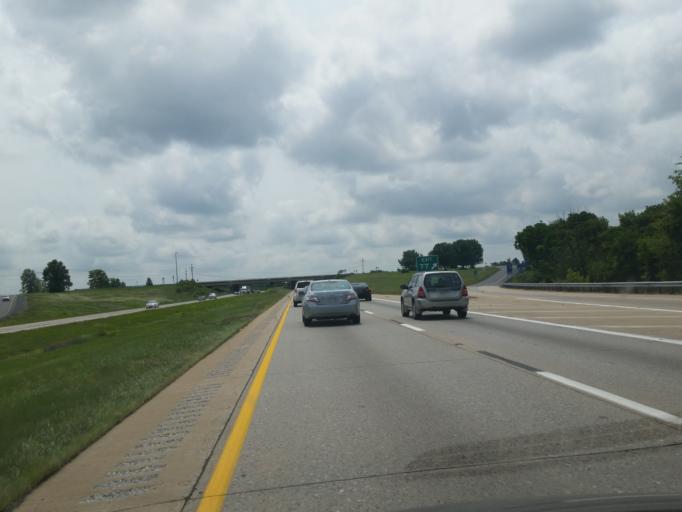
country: US
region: Pennsylvania
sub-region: Dauphin County
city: Skyline View
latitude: 40.3555
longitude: -76.7170
